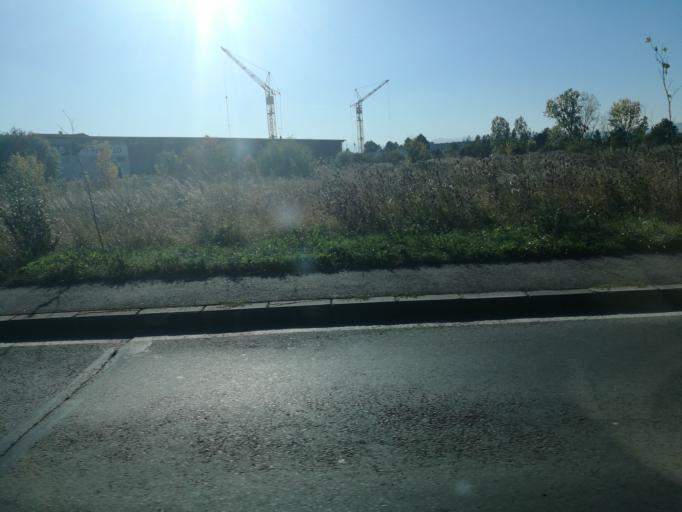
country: RO
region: Brasov
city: Brasov
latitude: 45.6773
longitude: 25.5878
